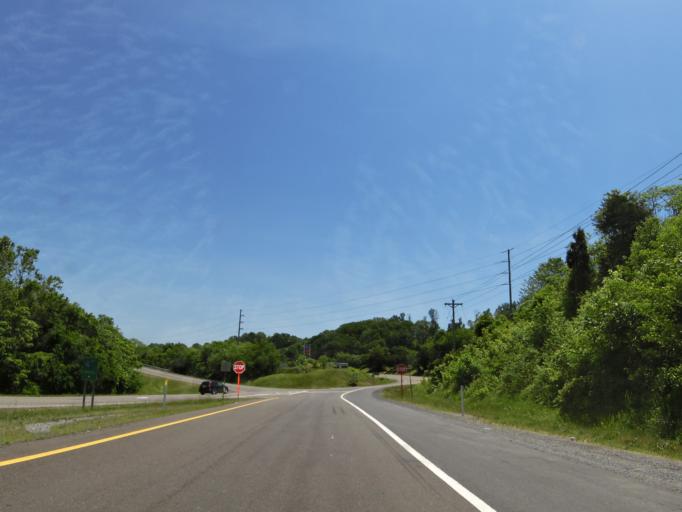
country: US
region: Tennessee
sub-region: Jefferson County
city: Dandridge
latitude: 36.0220
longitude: -83.4757
